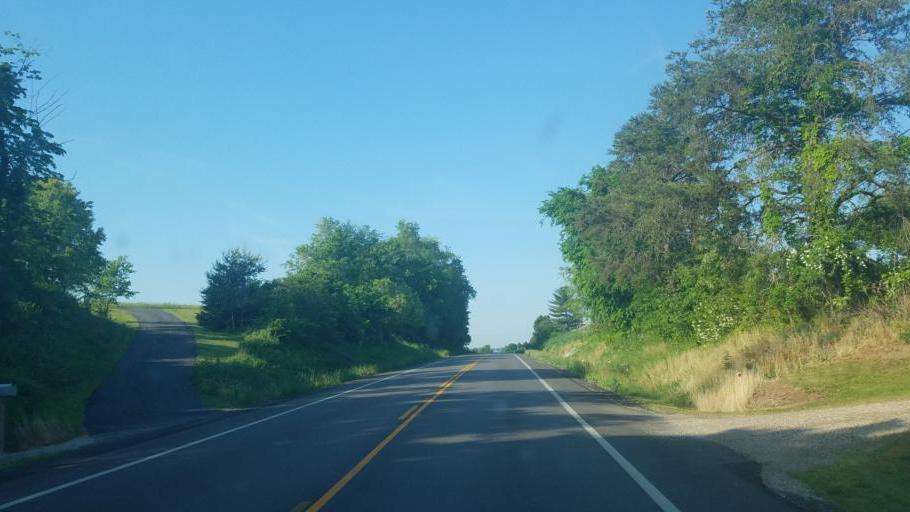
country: US
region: West Virginia
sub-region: Mason County
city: New Haven
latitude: 39.0799
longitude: -81.9285
